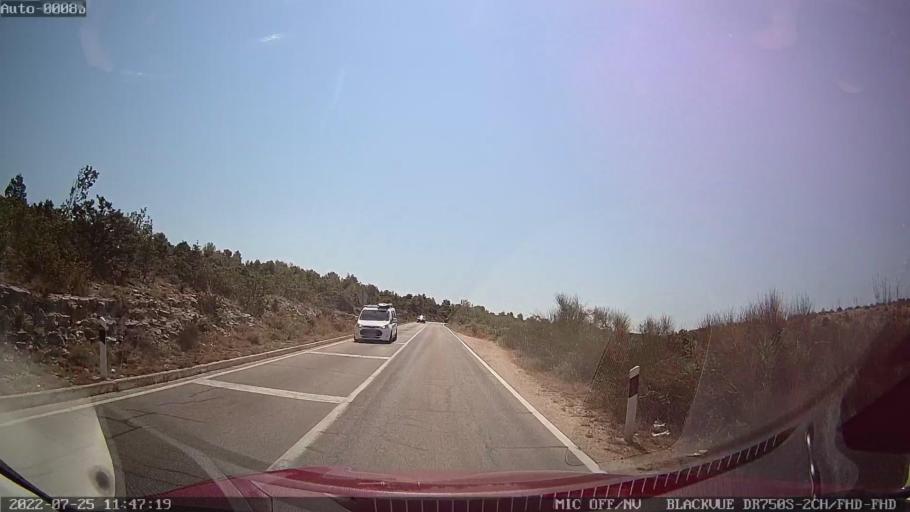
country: HR
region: Zadarska
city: Razanac
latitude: 44.2390
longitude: 15.3006
